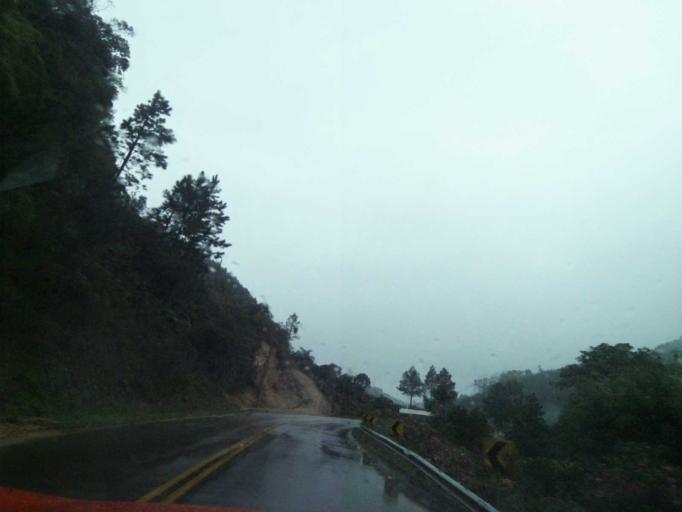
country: BR
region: Santa Catarina
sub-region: Anitapolis
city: Anitapolis
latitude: -27.8333
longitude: -49.0518
